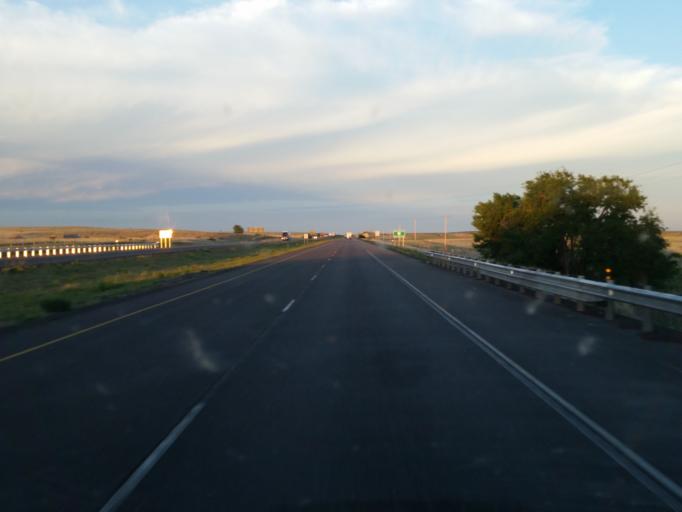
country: US
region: New Mexico
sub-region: San Miguel County
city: Las Vegas
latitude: 34.9910
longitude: -105.2874
